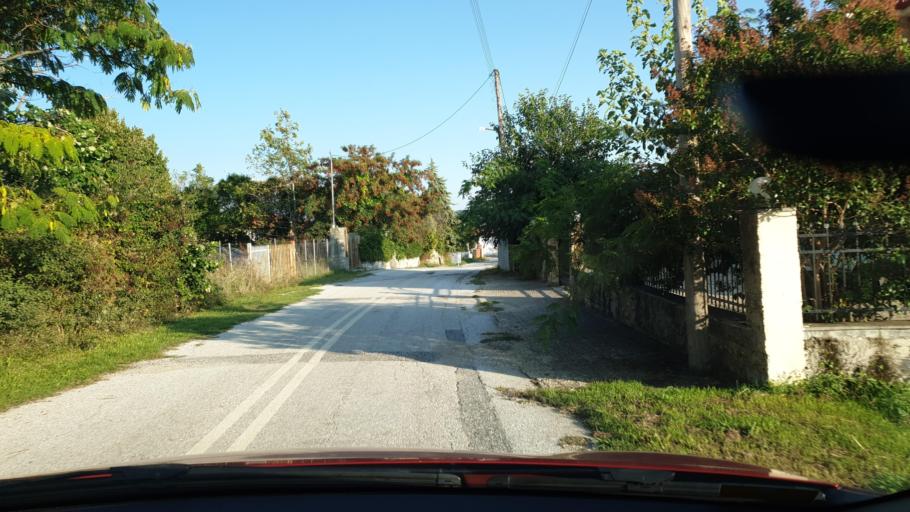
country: GR
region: Central Macedonia
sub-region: Nomos Chalkidikis
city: Galatista
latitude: 40.5174
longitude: 23.2820
